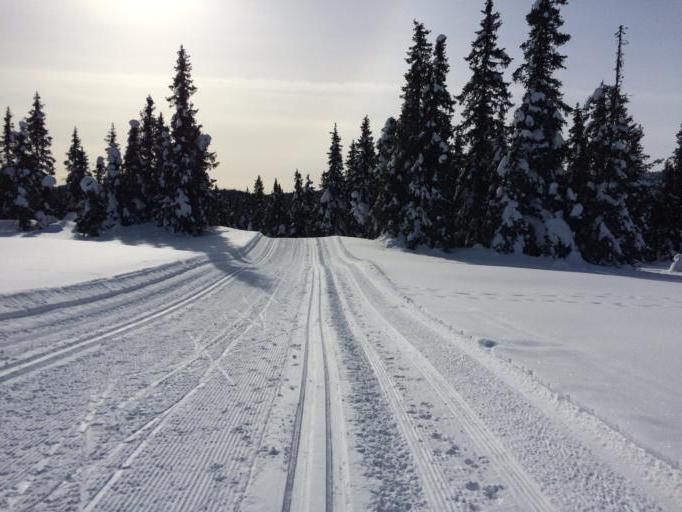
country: NO
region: Oppland
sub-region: Gausdal
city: Segalstad bru
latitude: 61.3310
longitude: 10.0837
